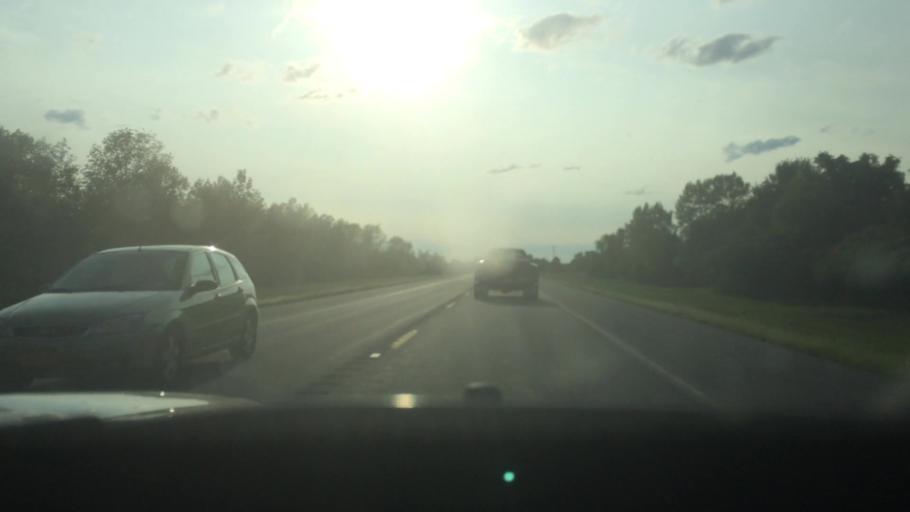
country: US
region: New York
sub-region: St. Lawrence County
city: Ogdensburg
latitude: 44.6792
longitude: -75.5095
